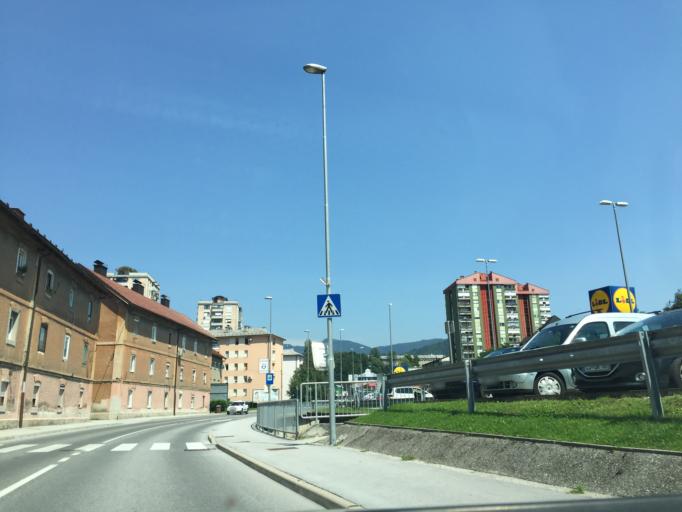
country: SI
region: Trbovlje
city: Trbovlje
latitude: 46.1451
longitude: 15.0380
